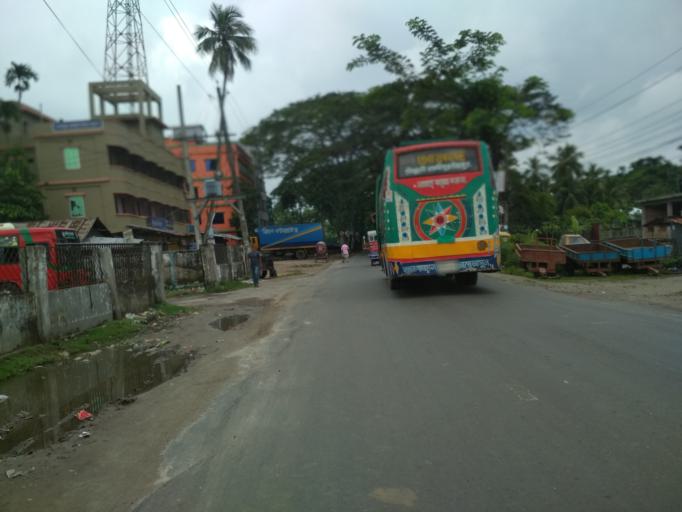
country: BD
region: Chittagong
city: Lakshmipur
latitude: 22.9464
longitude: 90.8123
